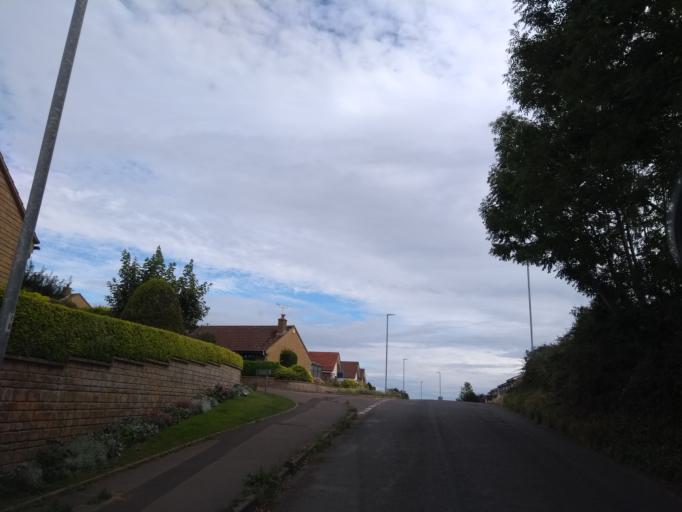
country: GB
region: England
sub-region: Somerset
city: Crewkerne
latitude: 50.8732
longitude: -2.7950
